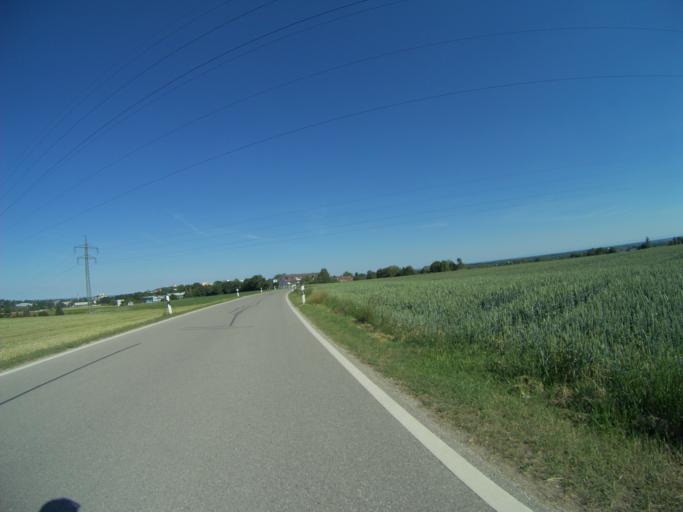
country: DE
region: Bavaria
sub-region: Upper Bavaria
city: Freising
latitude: 48.3992
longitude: 11.7039
